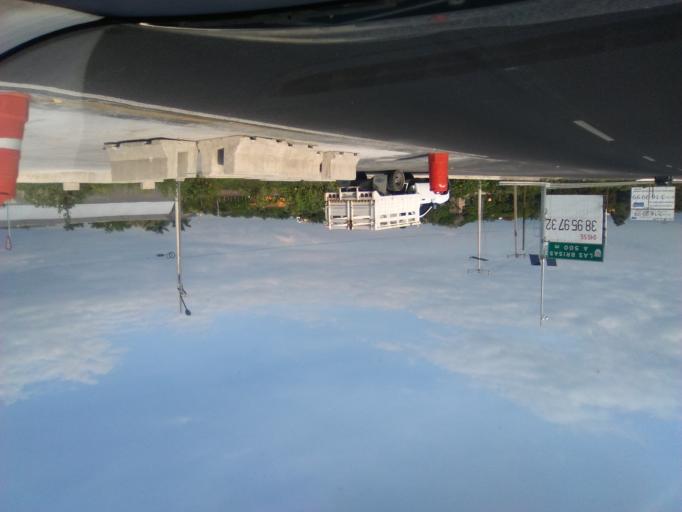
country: MX
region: Morelos
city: Temixco
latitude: 18.8385
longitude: -99.2171
